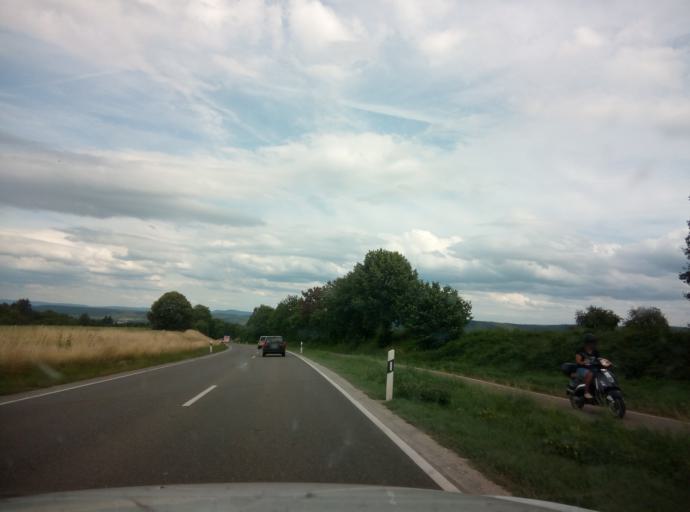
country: DE
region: Baden-Wuerttemberg
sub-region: Tuebingen Region
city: Rottenburg
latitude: 48.4884
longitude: 8.9248
